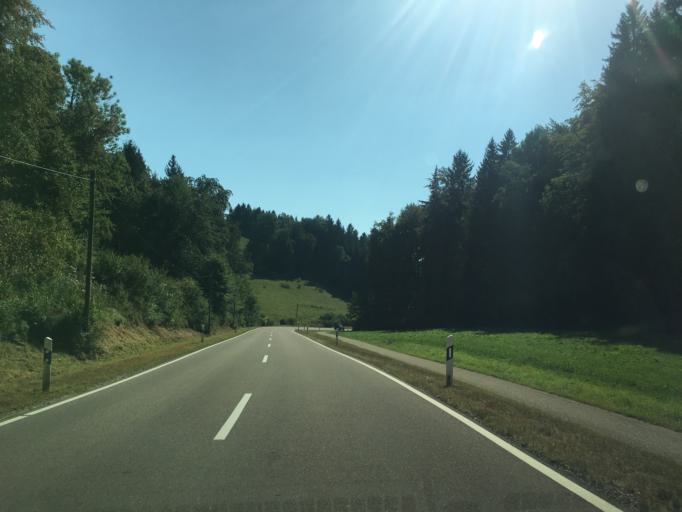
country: DE
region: Baden-Wuerttemberg
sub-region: Tuebingen Region
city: Munsingen
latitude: 48.3815
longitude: 9.4859
